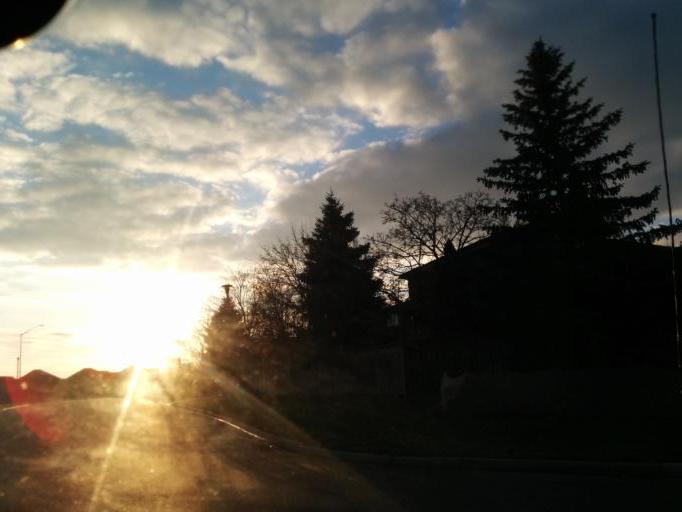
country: CA
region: Ontario
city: Brampton
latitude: 43.8754
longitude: -79.7537
